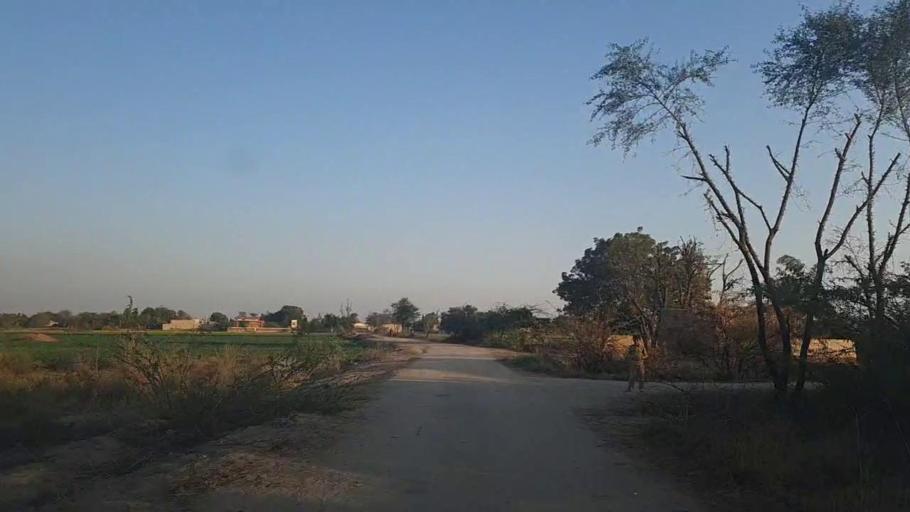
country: PK
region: Sindh
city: Jam Sahib
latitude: 26.3228
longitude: 68.6995
